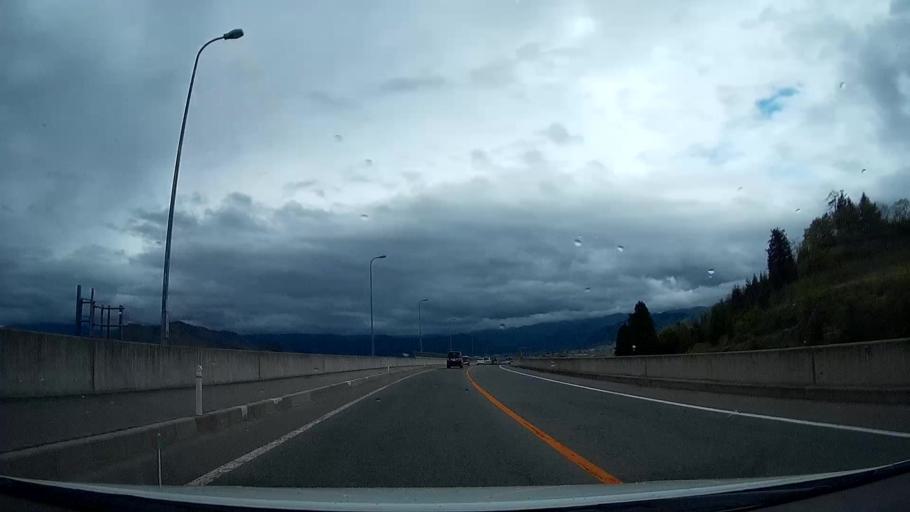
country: JP
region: Yamagata
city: Kaminoyama
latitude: 38.1304
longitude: 140.2479
